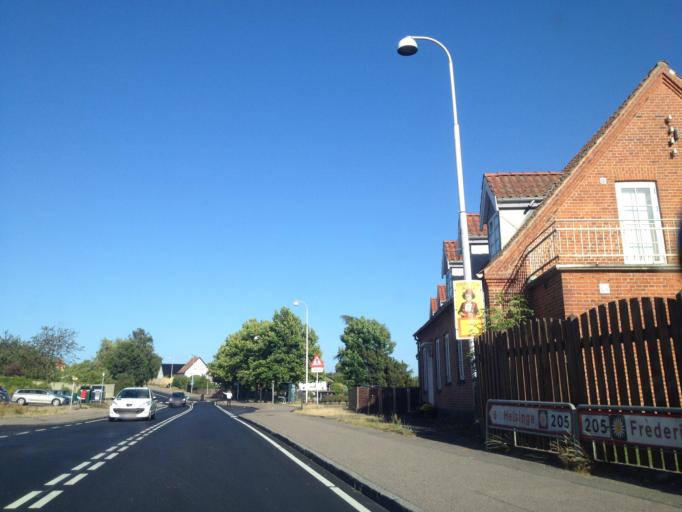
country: DK
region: Capital Region
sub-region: Gribskov Kommune
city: Helsinge
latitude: 56.0154
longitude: 12.1142
